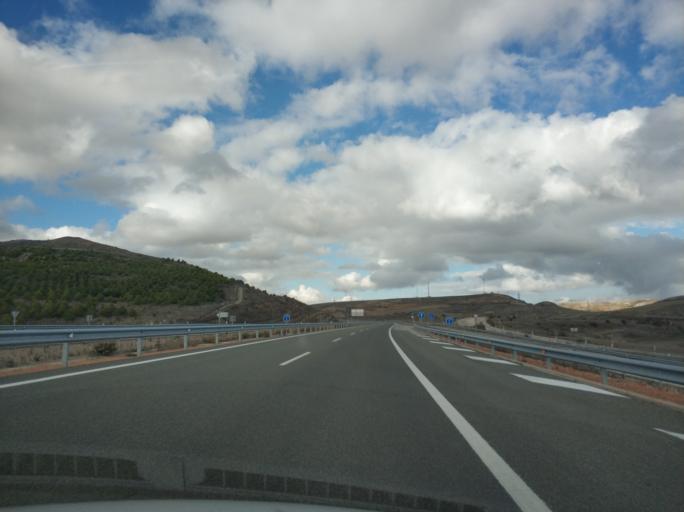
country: ES
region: Castille and Leon
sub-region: Provincia de Soria
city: Yelo
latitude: 41.2198
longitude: -2.4716
